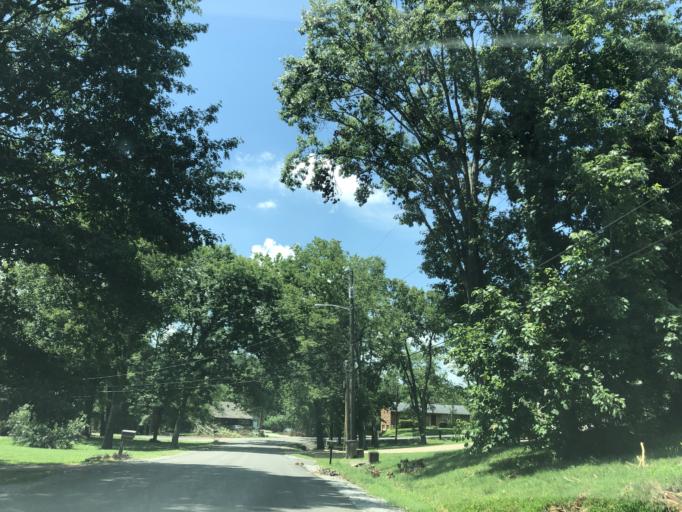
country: US
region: Tennessee
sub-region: Davidson County
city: Lakewood
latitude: 36.1787
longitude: -86.6503
